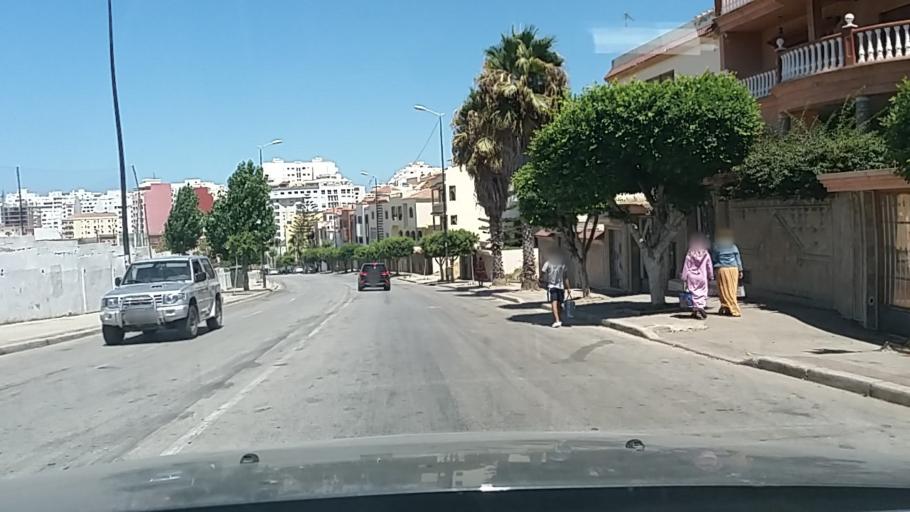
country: MA
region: Tanger-Tetouan
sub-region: Tanger-Assilah
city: Tangier
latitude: 35.7689
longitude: -5.7936
